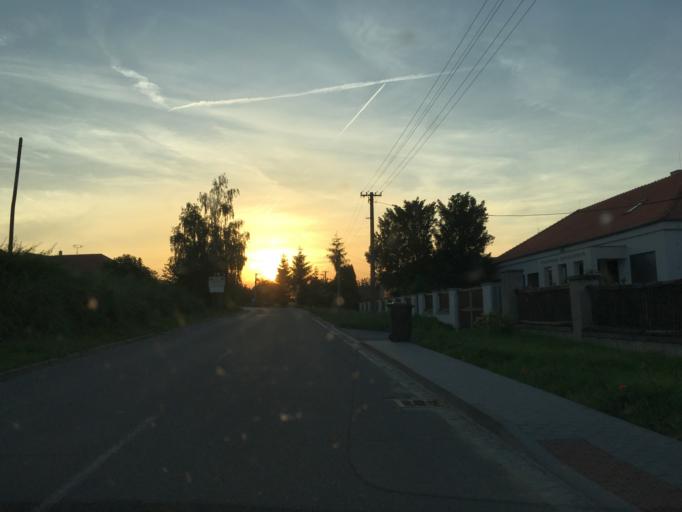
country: CZ
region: South Moravian
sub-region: Okres Breclav
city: Valtice
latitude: 48.7410
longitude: 16.7487
